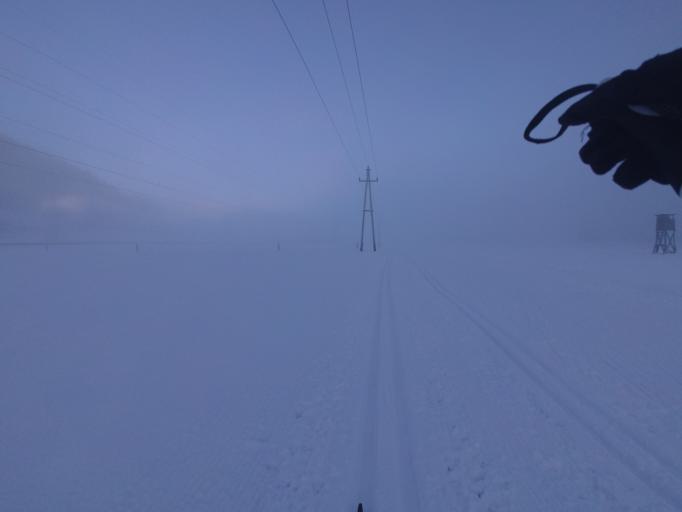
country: AT
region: Salzburg
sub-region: Politischer Bezirk Sankt Johann im Pongau
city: Flachau
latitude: 47.3588
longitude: 13.3581
